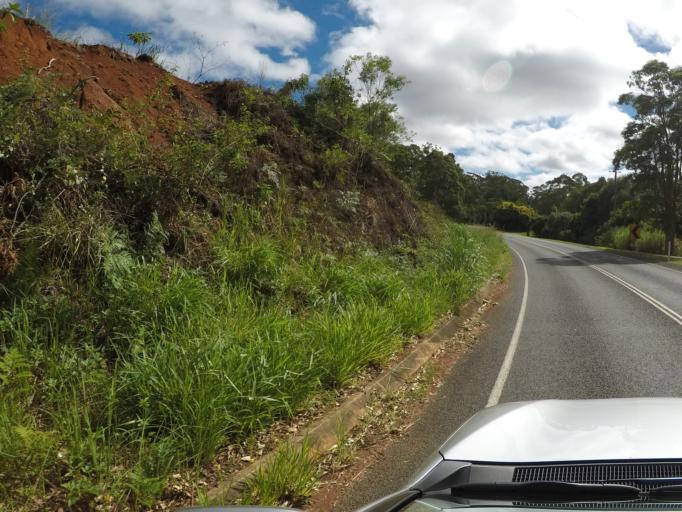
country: AU
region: Queensland
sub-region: Sunshine Coast
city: Nambour
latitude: -26.6327
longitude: 152.8579
